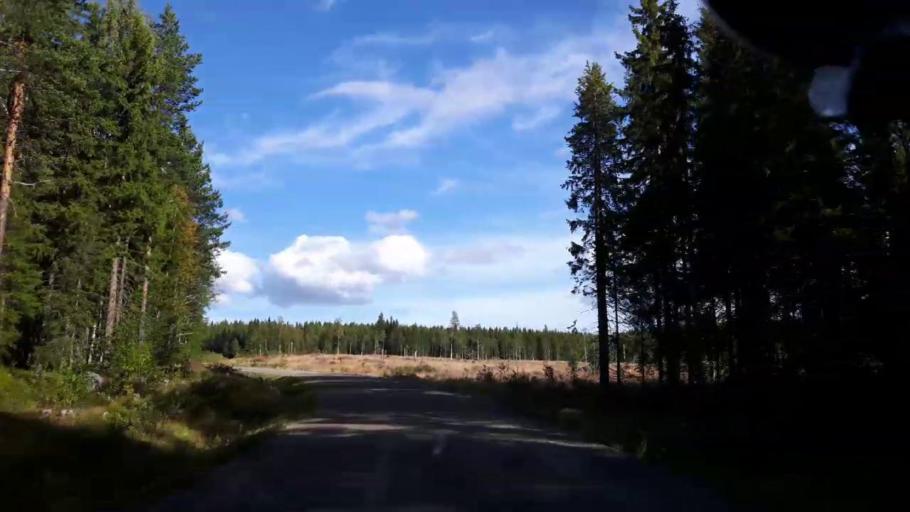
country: SE
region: Jaemtland
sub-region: Ragunda Kommun
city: Hammarstrand
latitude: 63.4418
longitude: 15.9582
